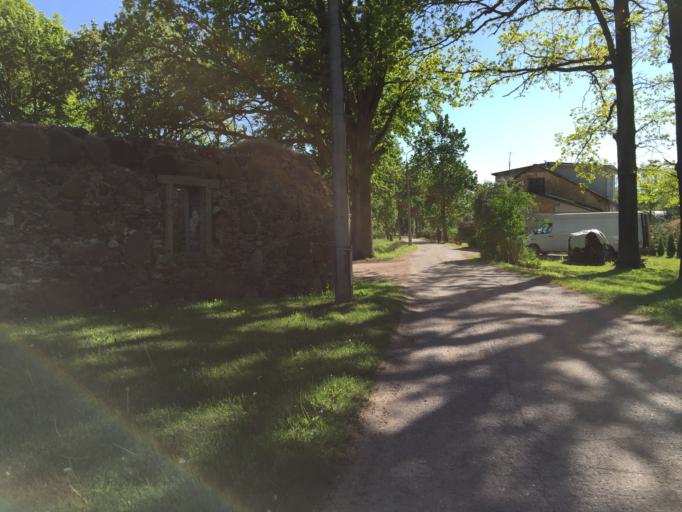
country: LV
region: Jelgava
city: Jelgava
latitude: 56.5215
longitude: 23.7557
